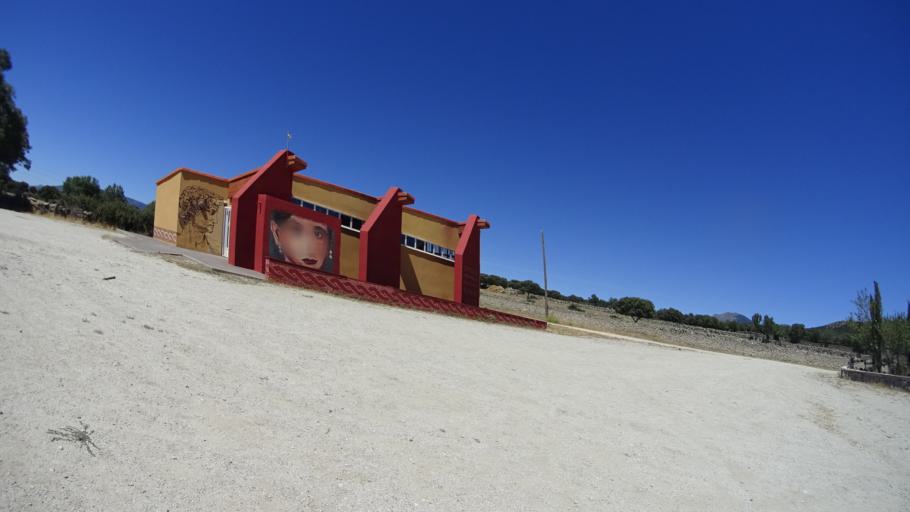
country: ES
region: Madrid
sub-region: Provincia de Madrid
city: Collado Mediano
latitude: 40.6844
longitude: -4.0353
